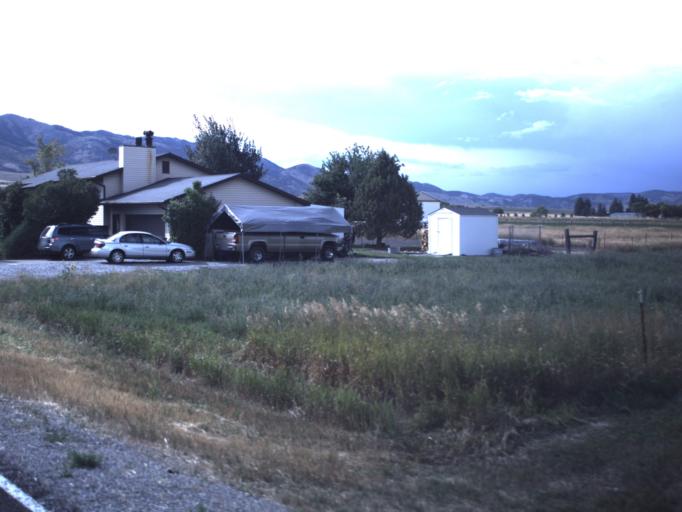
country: US
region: Utah
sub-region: Cache County
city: Benson
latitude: 41.9199
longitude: -112.0391
